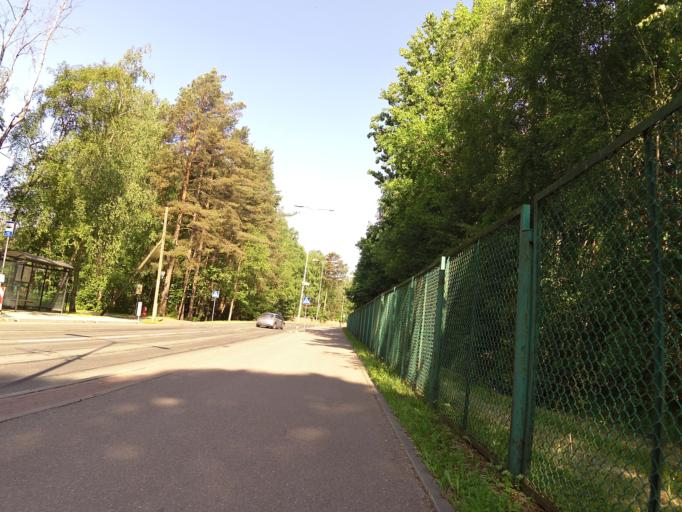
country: EE
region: Harju
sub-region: Saue vald
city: Laagri
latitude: 59.4333
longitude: 24.6313
